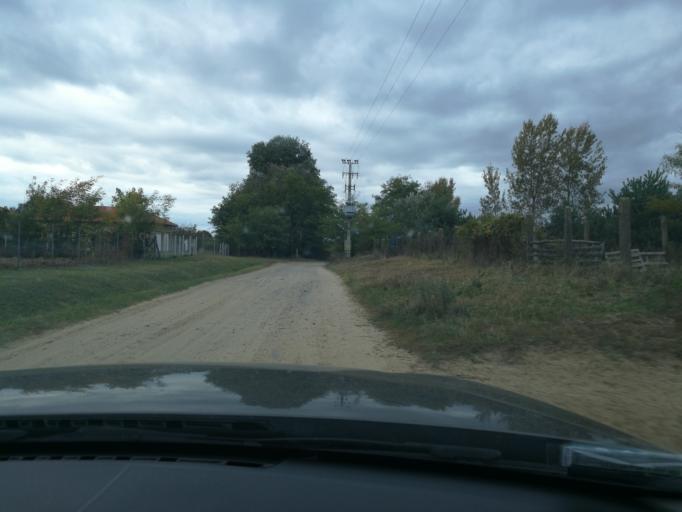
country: HU
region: Szabolcs-Szatmar-Bereg
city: Nyirpazony
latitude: 47.9981
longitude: 21.8006
